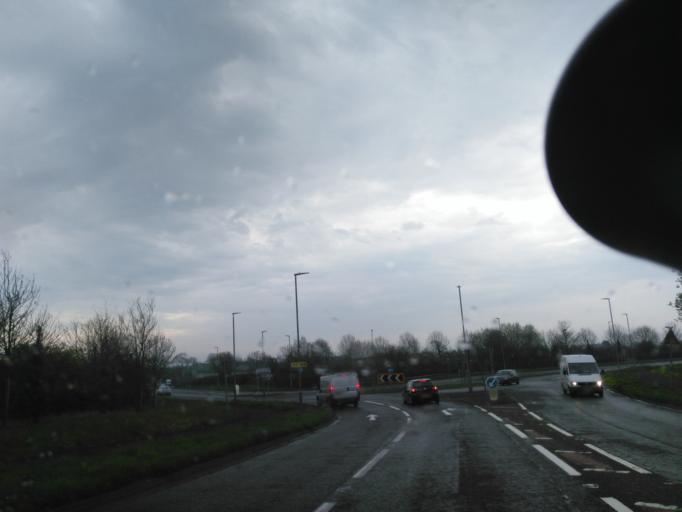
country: GB
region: England
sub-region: Somerset
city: Shepton Mallet
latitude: 51.1708
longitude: -2.5343
